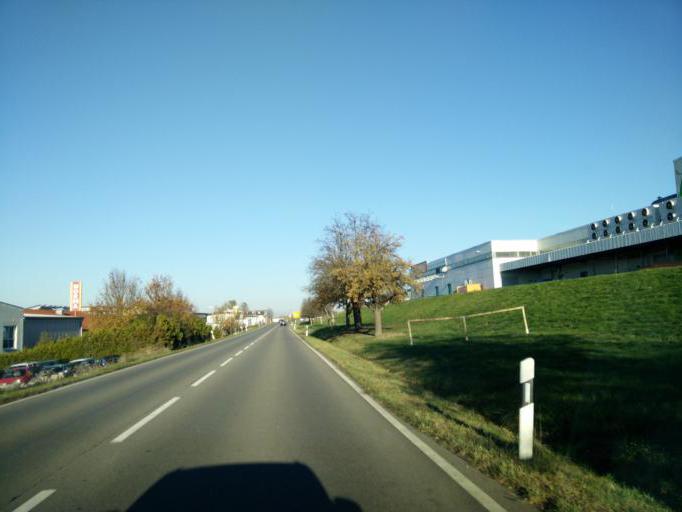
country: DE
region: Baden-Wuerttemberg
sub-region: Tuebingen Region
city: Gomaringen
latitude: 48.4598
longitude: 9.1019
